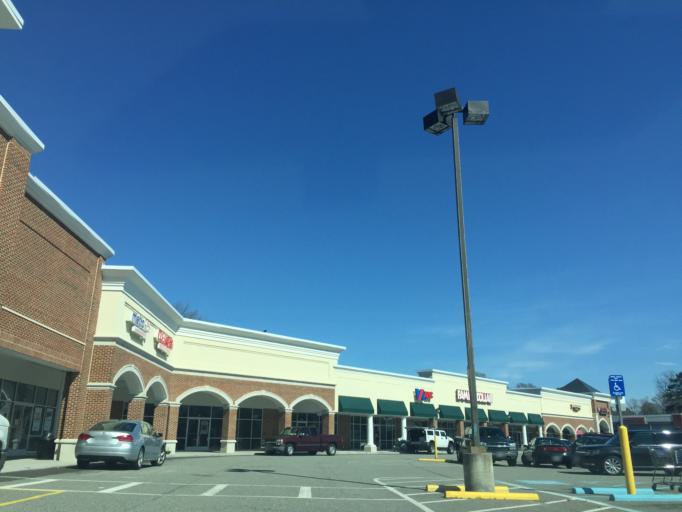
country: US
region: Virginia
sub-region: City of Newport News
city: Newport News
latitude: 37.0705
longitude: -76.4947
